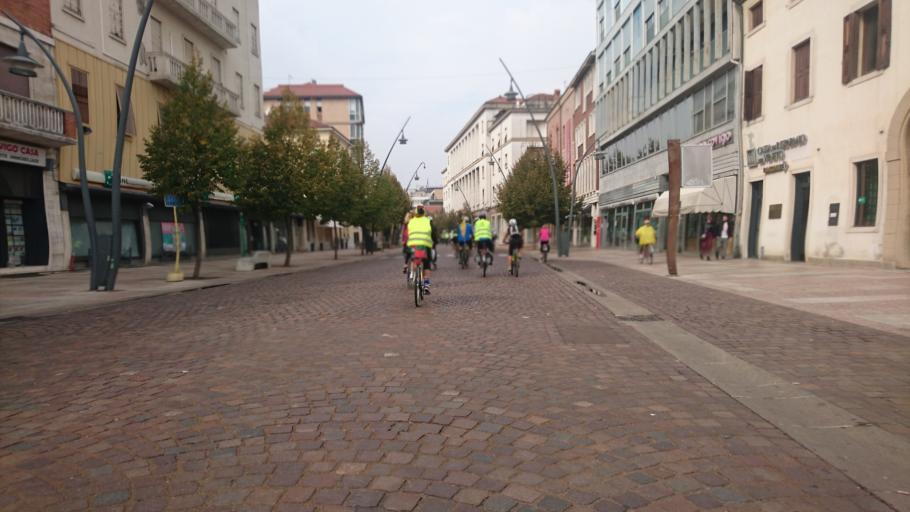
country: IT
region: Veneto
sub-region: Provincia di Rovigo
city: Rovigo
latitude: 45.0699
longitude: 11.7902
